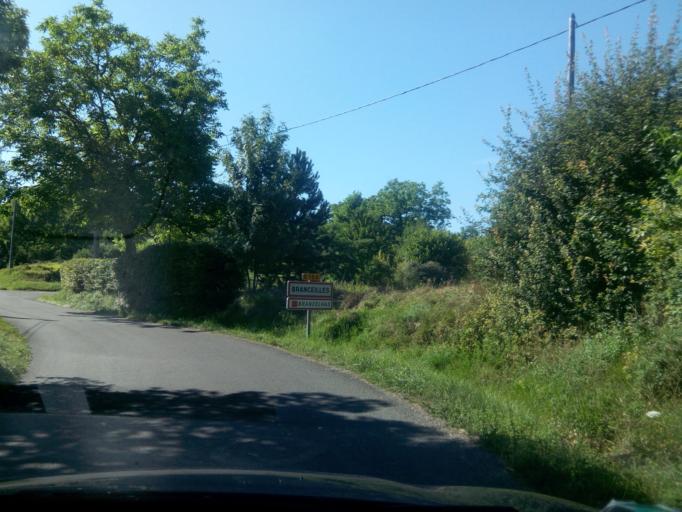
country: FR
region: Midi-Pyrenees
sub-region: Departement du Lot
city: Vayrac
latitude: 45.0110
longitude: 1.7123
